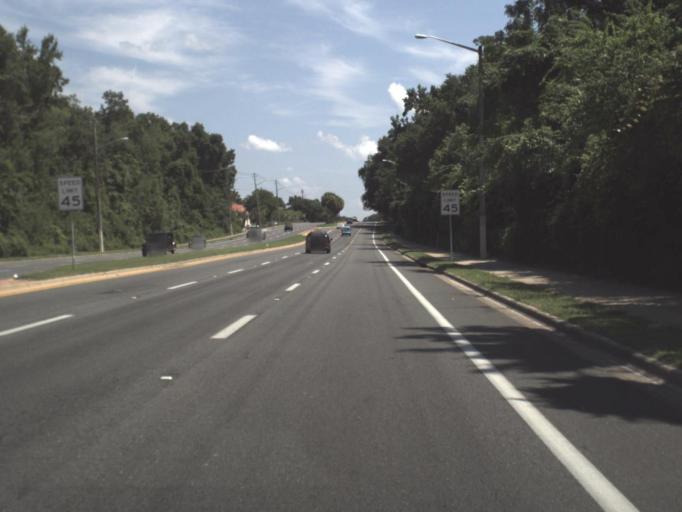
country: US
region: Florida
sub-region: Alachua County
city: Gainesville
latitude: 29.6428
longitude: -82.3724
